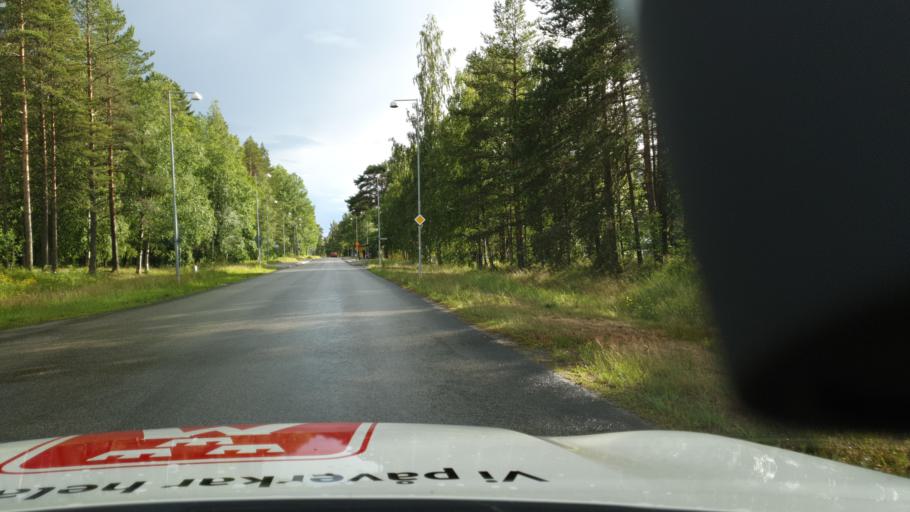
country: SE
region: Vaesterbotten
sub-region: Umea Kommun
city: Umea
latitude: 63.8477
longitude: 20.2956
